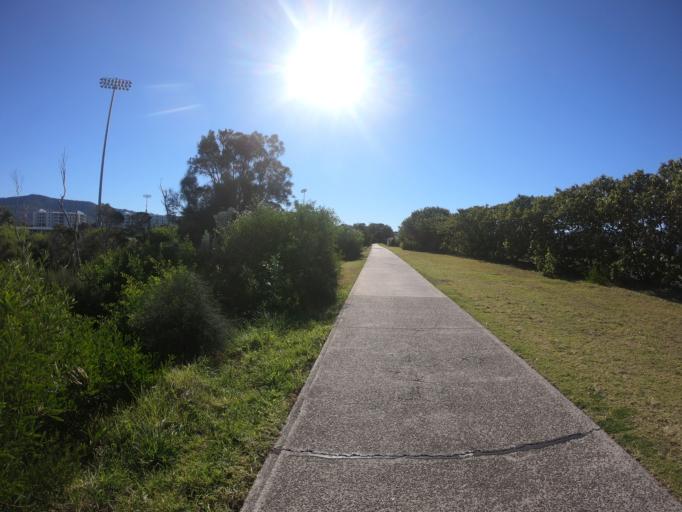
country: AU
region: New South Wales
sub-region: Wollongong
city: Fairy Meadow
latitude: -34.3927
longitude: 150.9057
